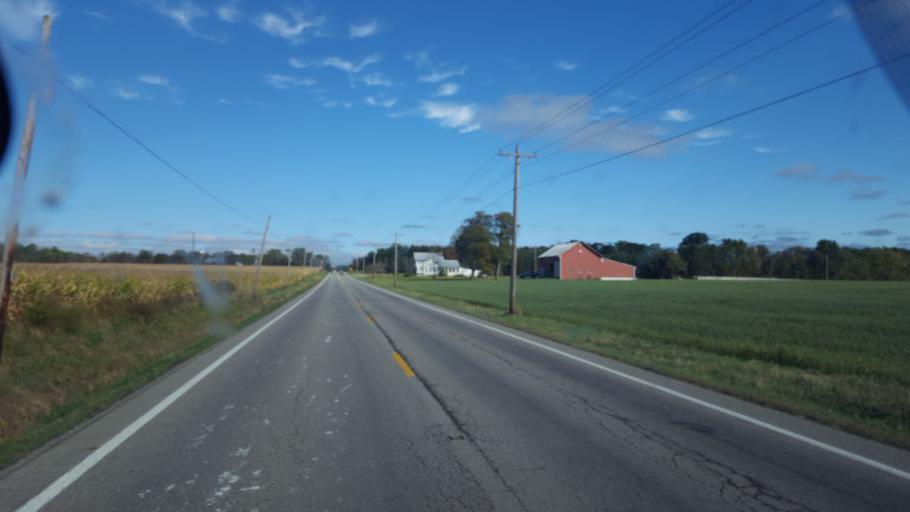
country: US
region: Ohio
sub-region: Huron County
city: Greenwich
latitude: 41.0813
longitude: -82.4873
